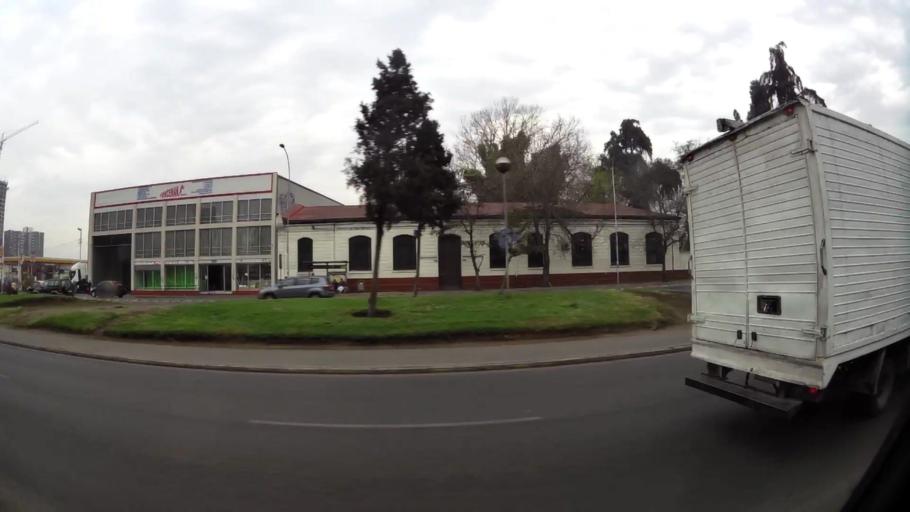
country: CL
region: Santiago Metropolitan
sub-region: Provincia de Santiago
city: Santiago
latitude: -33.4530
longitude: -70.6866
